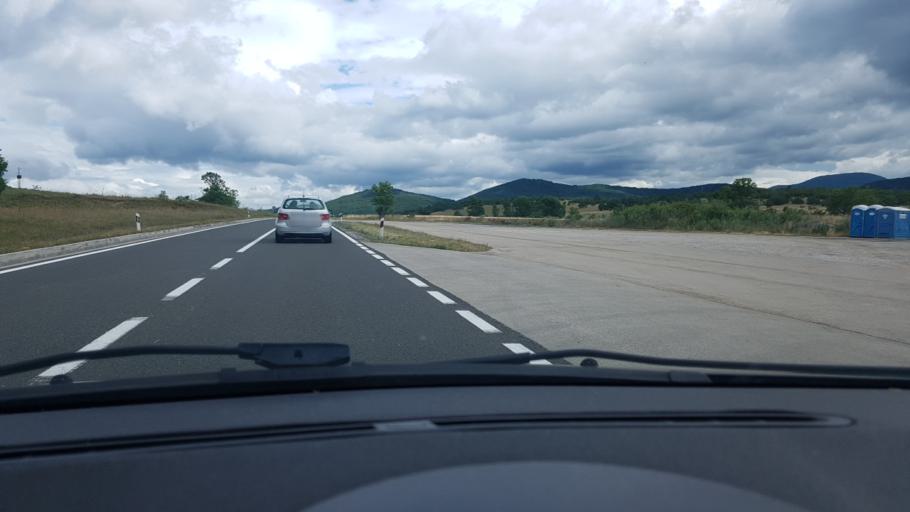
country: HR
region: Zadarska
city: Gracac
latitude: 44.4745
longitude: 15.7894
